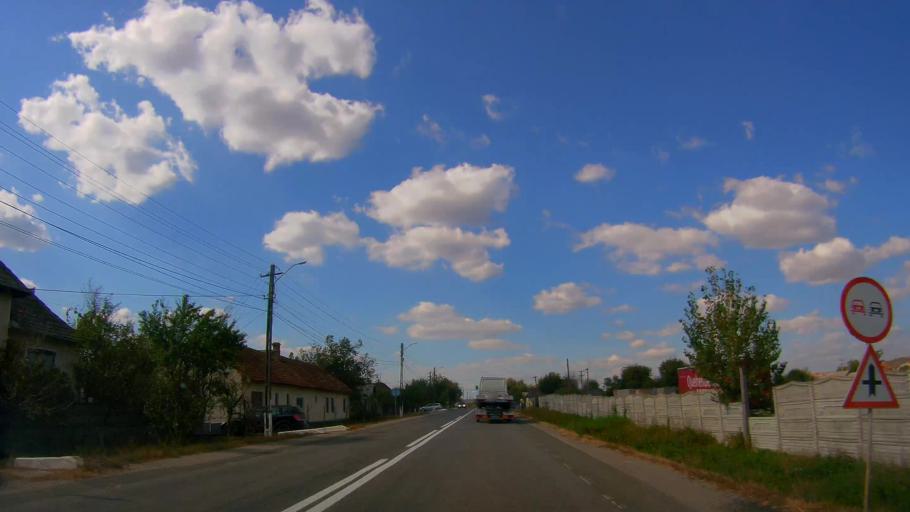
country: RO
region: Salaj
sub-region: Comuna Bobota
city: Bobota
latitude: 47.3778
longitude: 22.7850
